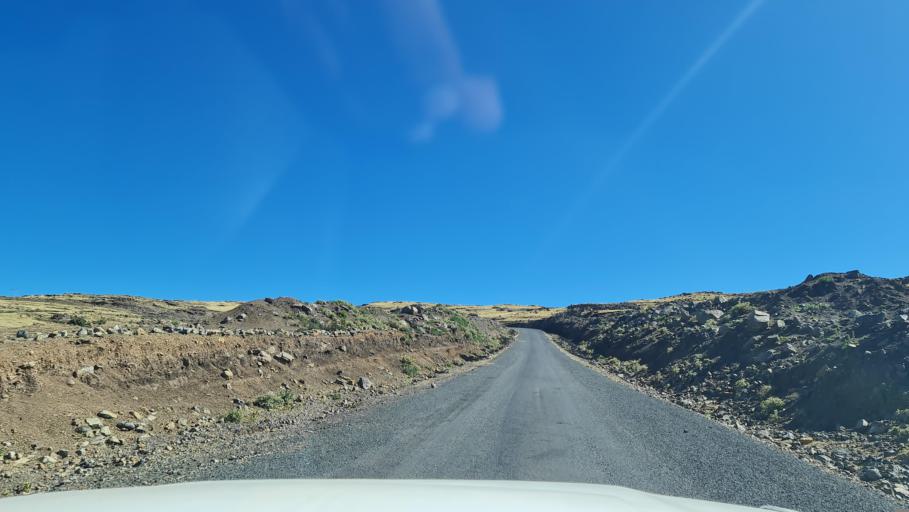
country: ET
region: Amhara
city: Debark'
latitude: 13.1485
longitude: 38.1847
